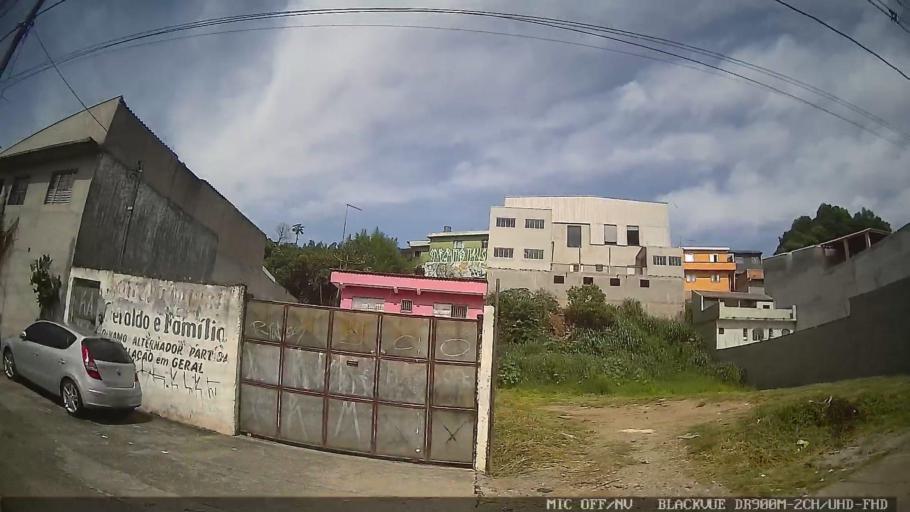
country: BR
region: Sao Paulo
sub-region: Suzano
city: Suzano
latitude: -23.5095
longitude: -46.3001
